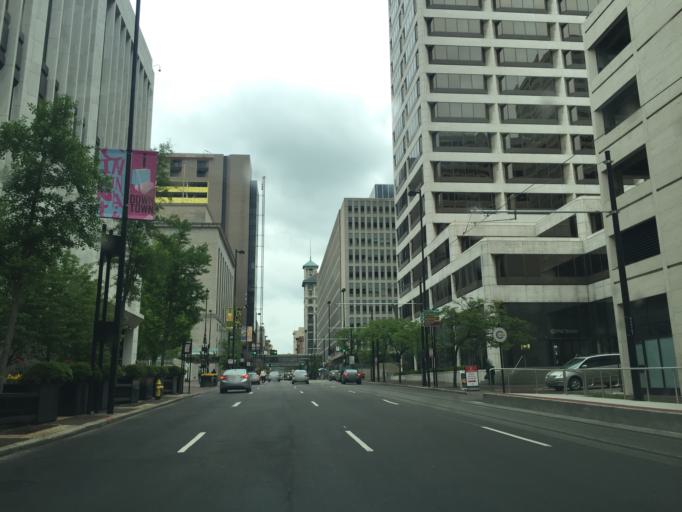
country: US
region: Kentucky
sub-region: Campbell County
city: Newport
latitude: 39.1006
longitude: -84.5096
